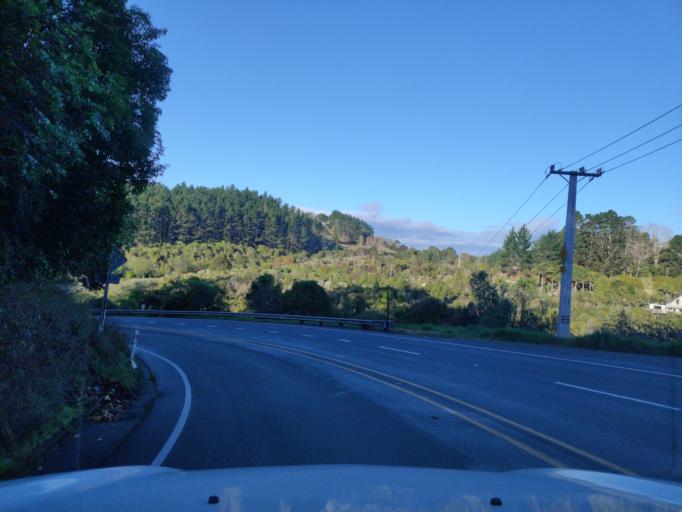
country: NZ
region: Auckland
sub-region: Auckland
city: Pakuranga
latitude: -36.9249
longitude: 174.9334
